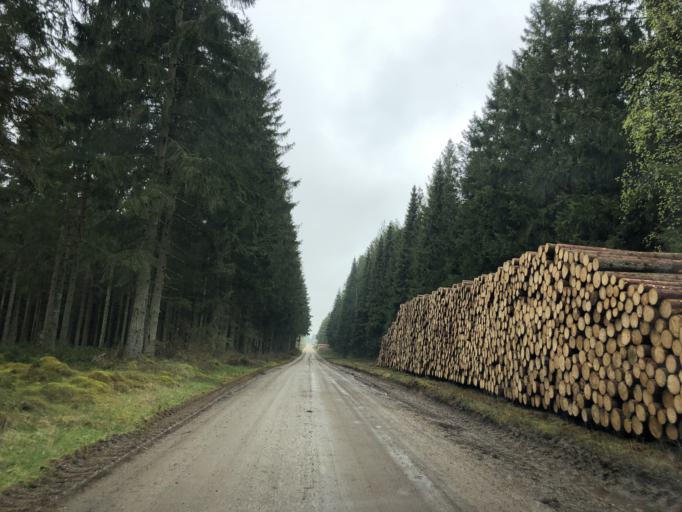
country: DK
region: Central Jutland
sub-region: Lemvig Kommune
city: Lemvig
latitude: 56.4896
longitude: 8.3521
